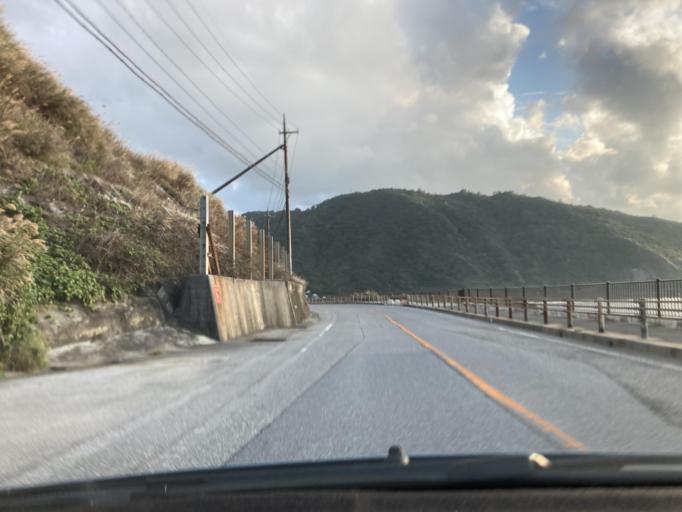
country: JP
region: Okinawa
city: Nago
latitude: 26.8027
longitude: 128.2310
